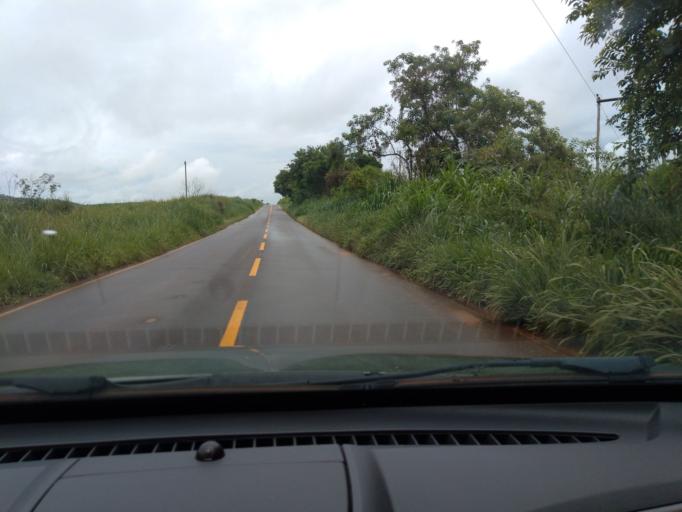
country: BR
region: Minas Gerais
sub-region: Tres Coracoes
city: Tres Coracoes
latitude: -21.6593
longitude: -45.1368
